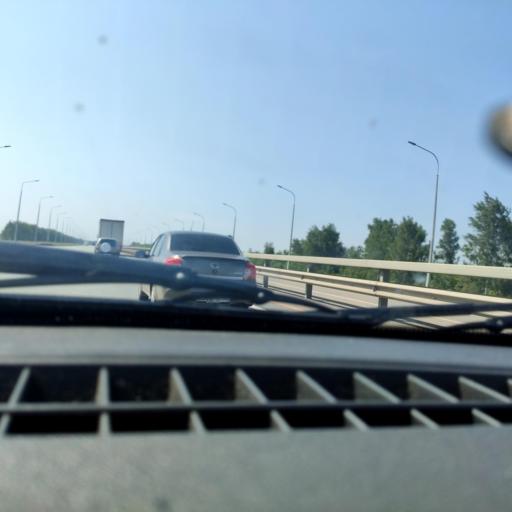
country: RU
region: Bashkortostan
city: Buzdyak
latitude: 54.6521
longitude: 54.6219
